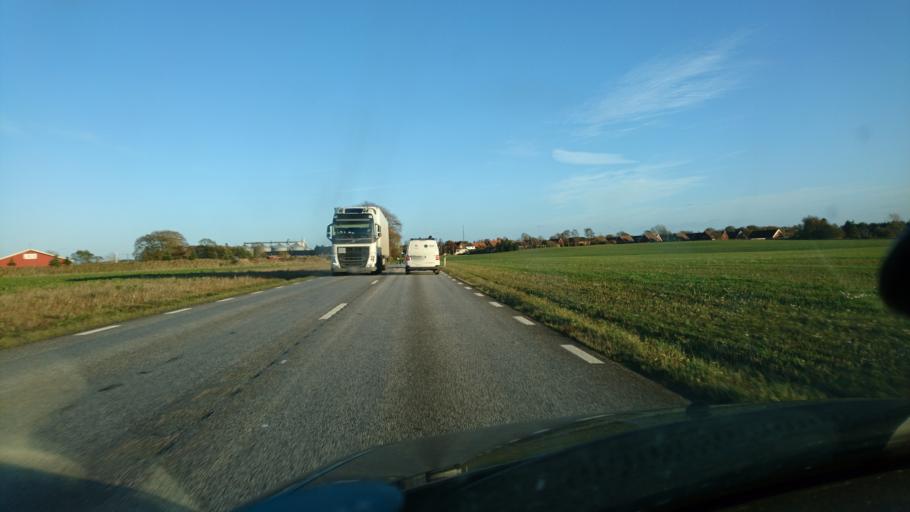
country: SE
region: Skane
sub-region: Tomelilla Kommun
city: Tomelilla
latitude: 55.5449
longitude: 14.0348
